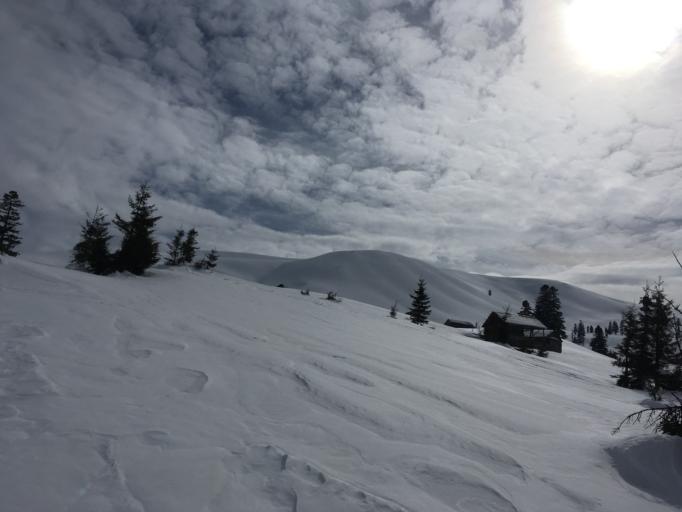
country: GE
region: Ajaria
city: Dioknisi
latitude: 41.6223
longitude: 42.4951
